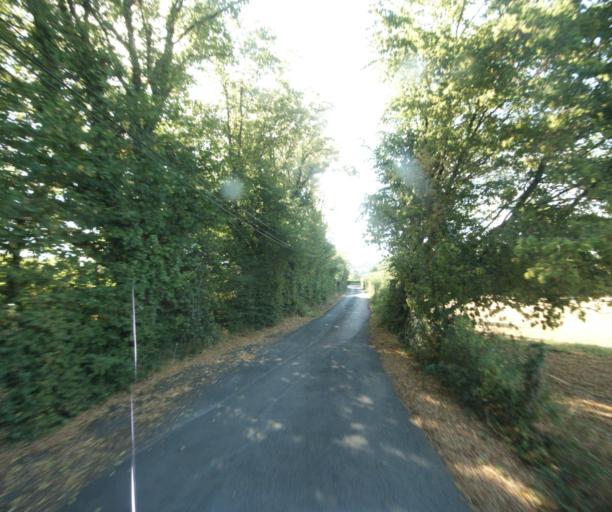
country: FR
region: Rhone-Alpes
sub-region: Departement du Rhone
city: Sainte-Consorce
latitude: 45.7999
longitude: 4.6889
